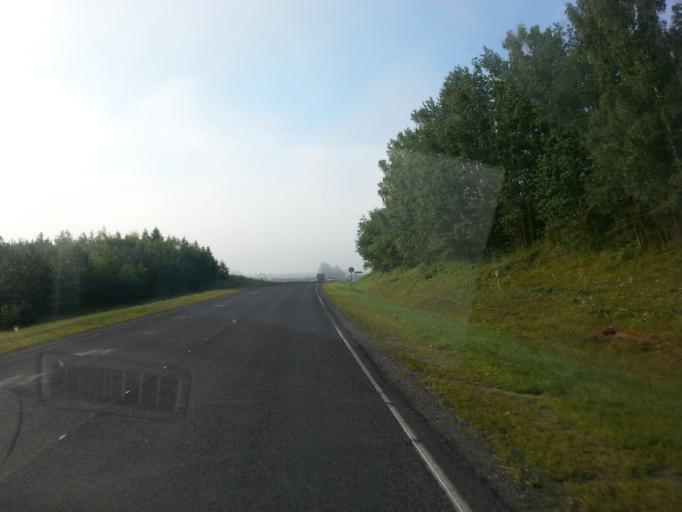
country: BY
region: Minsk
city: Kryvichy
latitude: 54.7363
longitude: 27.1344
